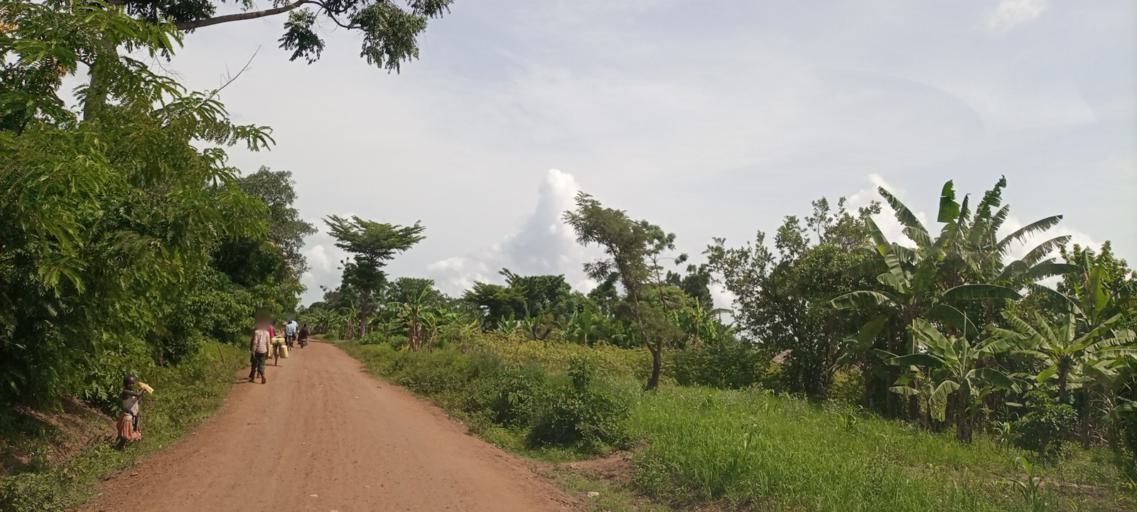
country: UG
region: Eastern Region
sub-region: Budaka District
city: Budaka
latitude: 1.1702
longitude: 33.9400
